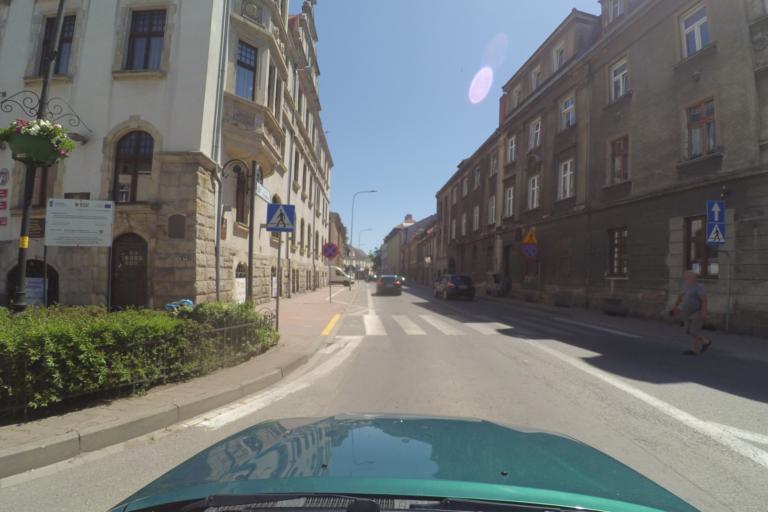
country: PL
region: Lower Silesian Voivodeship
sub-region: Powiat kamiennogorski
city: Kamienna Gora
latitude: 50.7823
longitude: 16.0308
